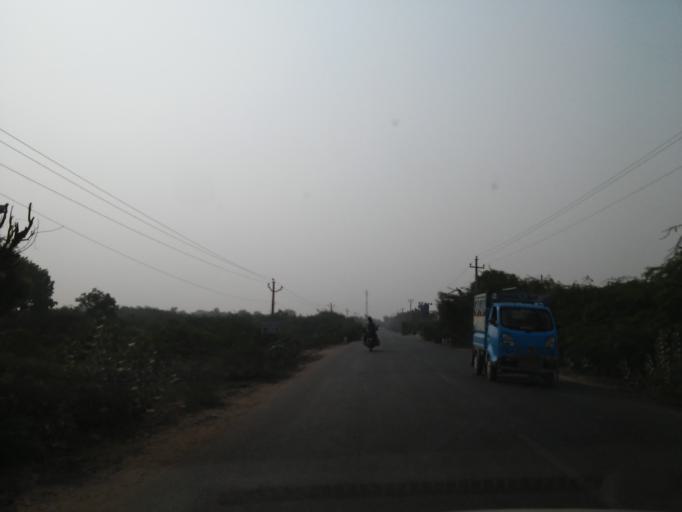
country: IN
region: Gujarat
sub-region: Kachchh
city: Bhuj
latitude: 23.8385
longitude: 69.7297
